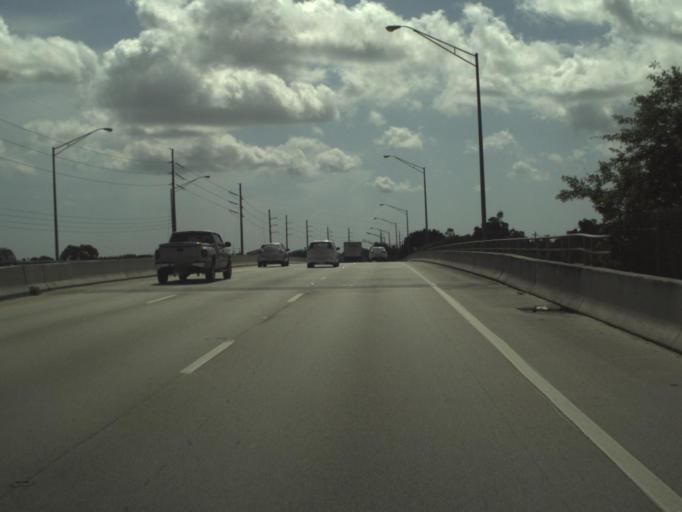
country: US
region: Florida
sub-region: Saint Lucie County
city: Port Saint Lucie
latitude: 27.2717
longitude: -80.3231
